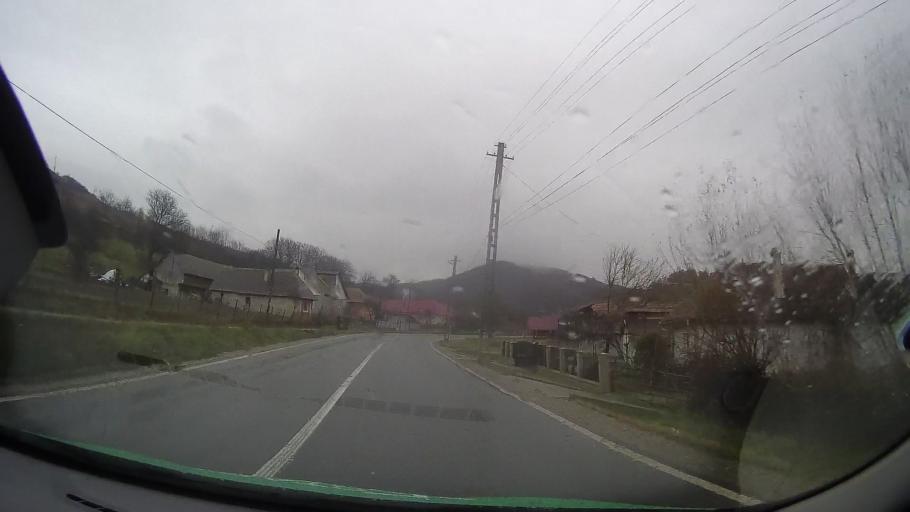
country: RO
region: Bistrita-Nasaud
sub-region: Comuna Galatii Bistritei
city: Galatii Bistritei
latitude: 46.9815
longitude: 24.4336
